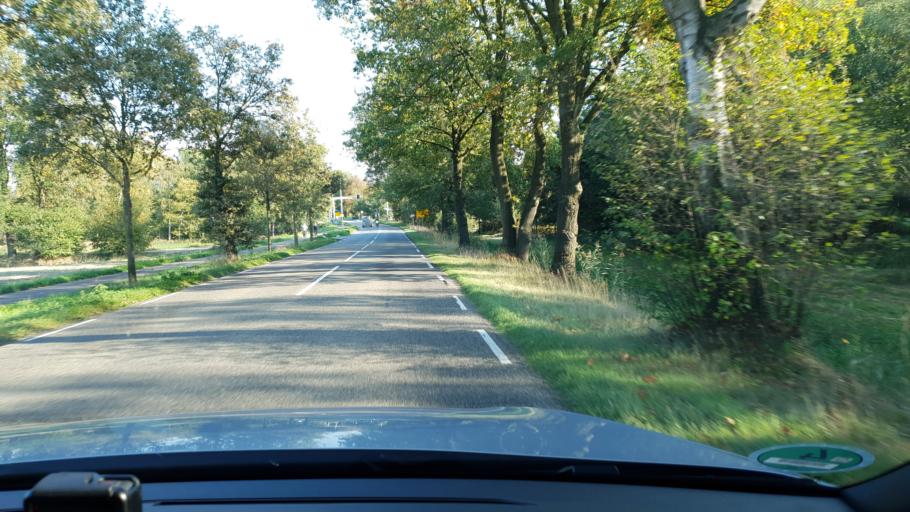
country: NL
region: North Brabant
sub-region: Gemeente Best
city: Best
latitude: 51.4719
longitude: 5.3892
